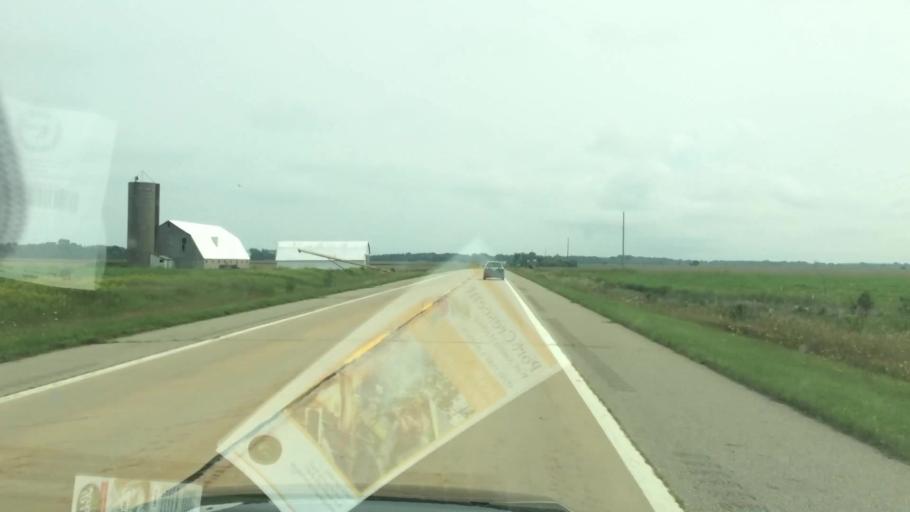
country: US
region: Michigan
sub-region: Huron County
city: Bad Axe
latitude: 44.0438
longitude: -82.9020
